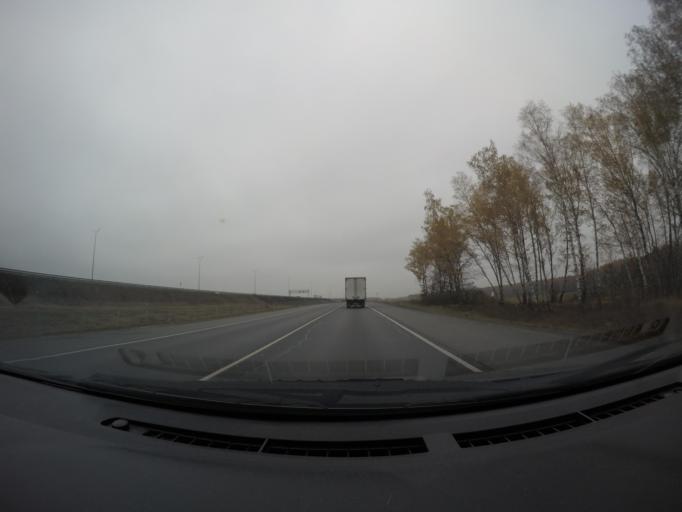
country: RU
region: Moskovskaya
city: Belyye Stolby
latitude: 55.3466
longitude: 37.8763
